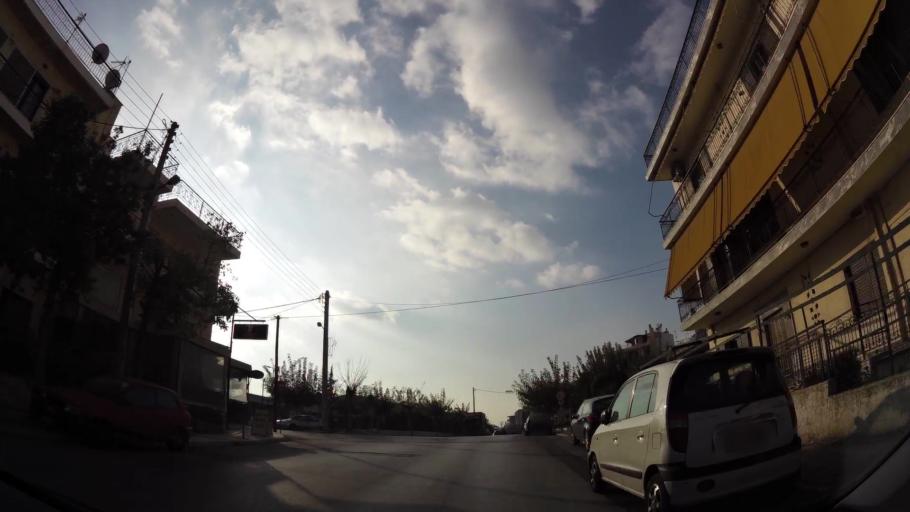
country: GR
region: Attica
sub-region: Nomarchia Anatolikis Attikis
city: Acharnes
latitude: 38.0742
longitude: 23.7428
